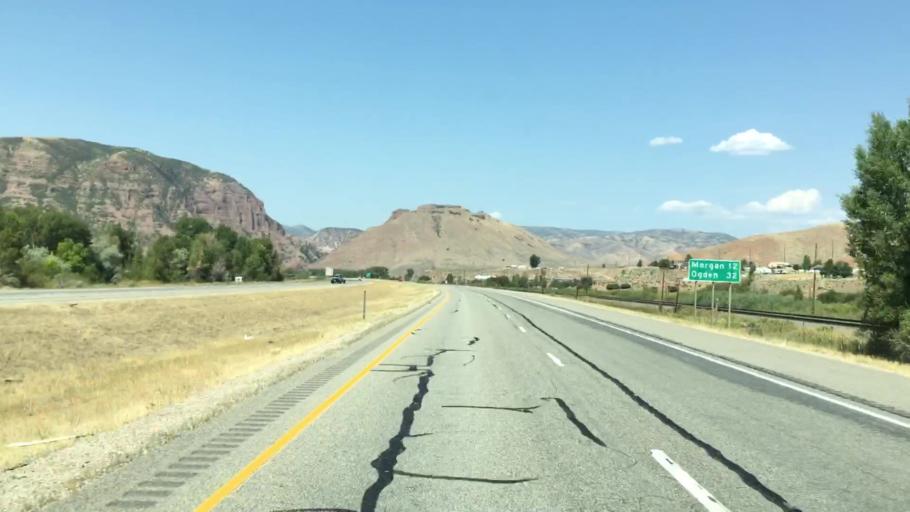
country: US
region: Utah
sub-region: Summit County
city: Coalville
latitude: 41.0265
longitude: -111.4983
